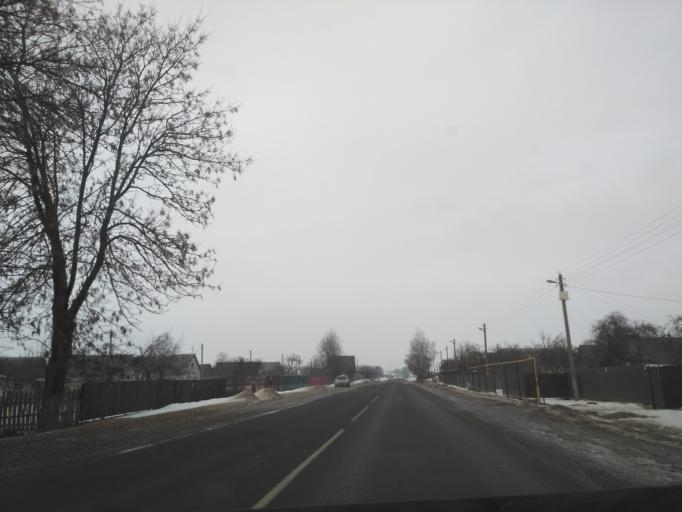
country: BY
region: Minsk
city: Horad Smalyavichy
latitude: 54.0266
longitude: 28.0638
